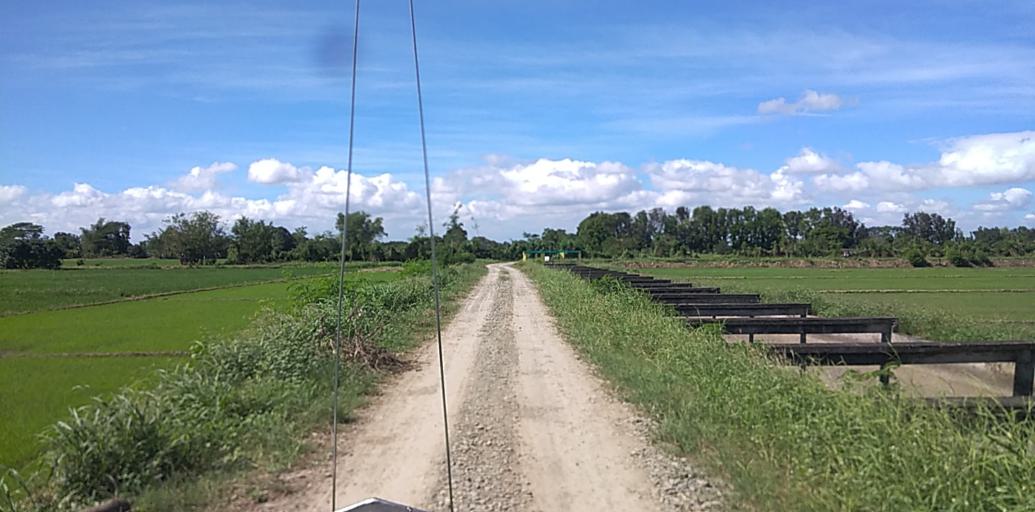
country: PH
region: Central Luzon
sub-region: Province of Pampanga
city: Candating
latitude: 15.1281
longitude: 120.7994
